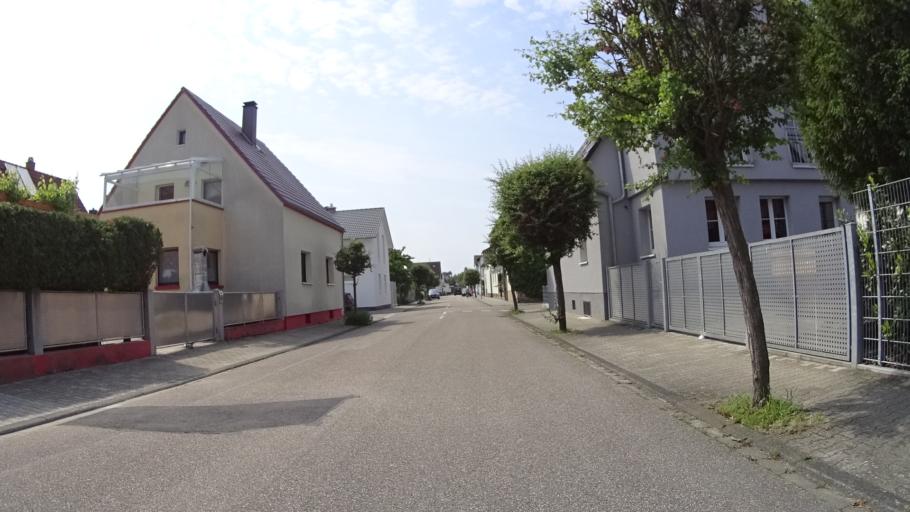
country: DE
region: Baden-Wuerttemberg
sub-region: Karlsruhe Region
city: Linkenheim-Hochstetten
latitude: 49.1248
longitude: 8.4156
